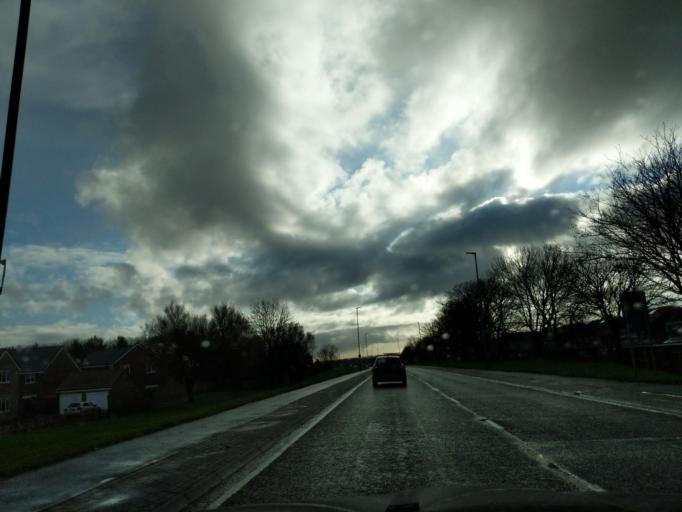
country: GB
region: England
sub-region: Northumberland
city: Blyth
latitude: 55.1136
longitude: -1.5059
